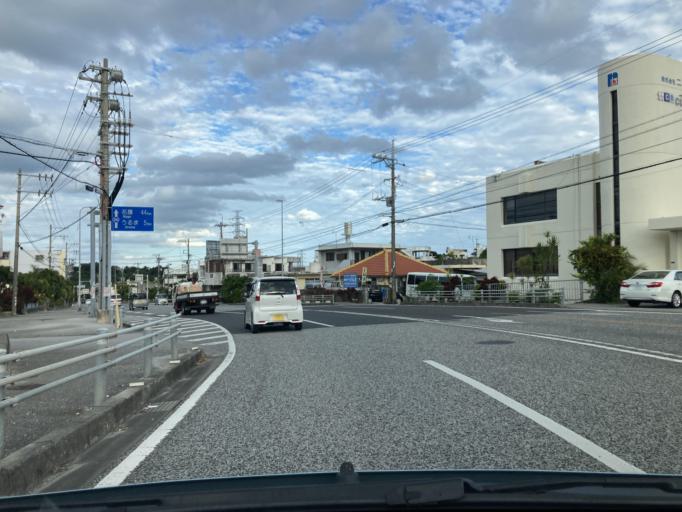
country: JP
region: Okinawa
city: Ishikawa
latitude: 26.3882
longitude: 127.8289
